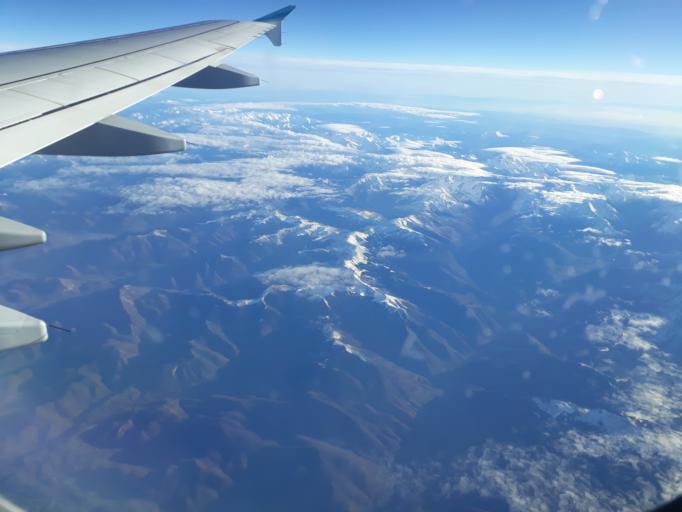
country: FR
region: Midi-Pyrenees
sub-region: Departement des Hautes-Pyrenees
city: Capvern
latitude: 43.1116
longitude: 0.3372
